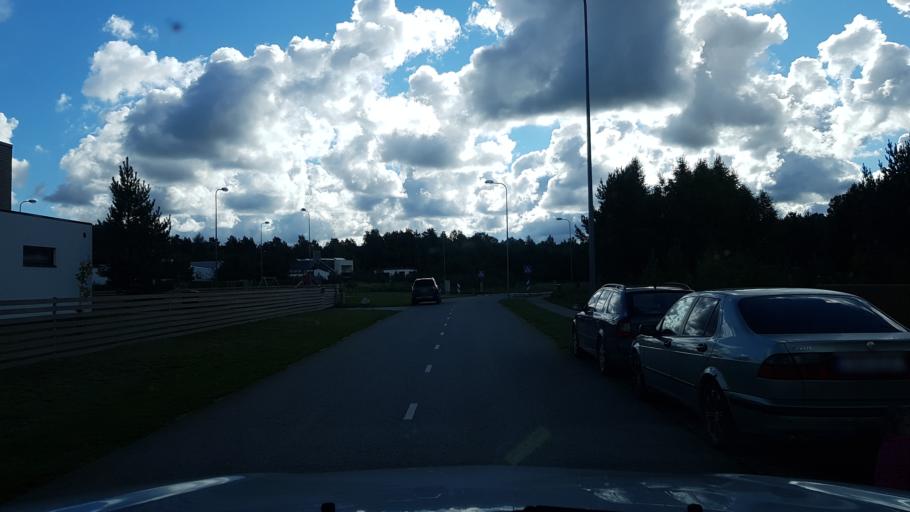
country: EE
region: Harju
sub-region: Tallinna linn
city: Tallinn
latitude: 59.3697
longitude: 24.7649
